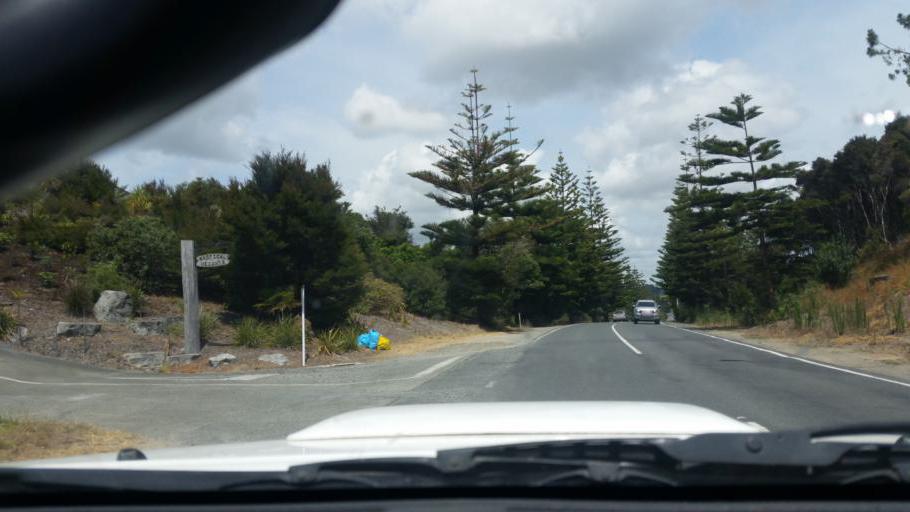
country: NZ
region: Auckland
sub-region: Auckland
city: Wellsford
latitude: -36.1037
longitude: 174.5855
